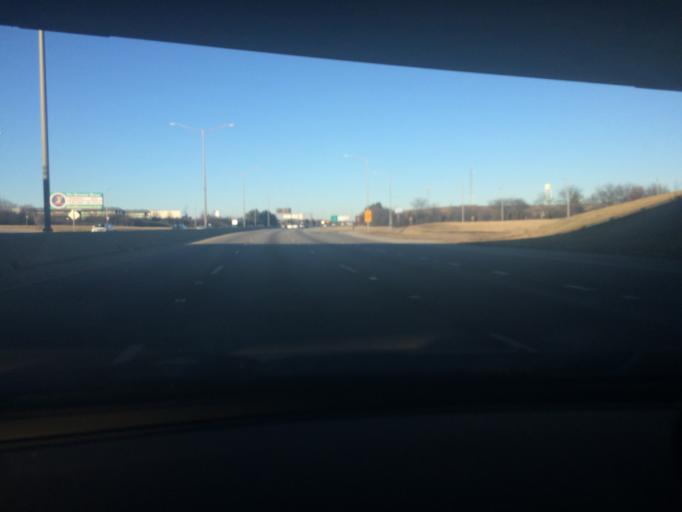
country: US
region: Illinois
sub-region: Cook County
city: Rolling Meadows
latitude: 42.0883
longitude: -88.0309
